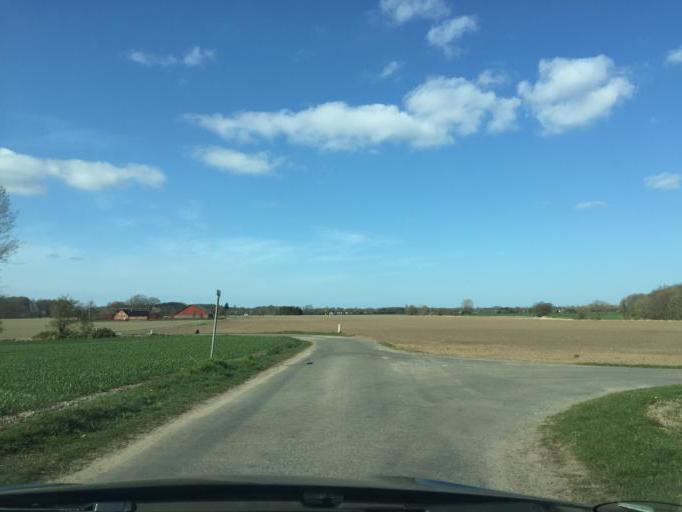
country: DK
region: South Denmark
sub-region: Faaborg-Midtfyn Kommune
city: Arslev
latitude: 55.2985
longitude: 10.5185
